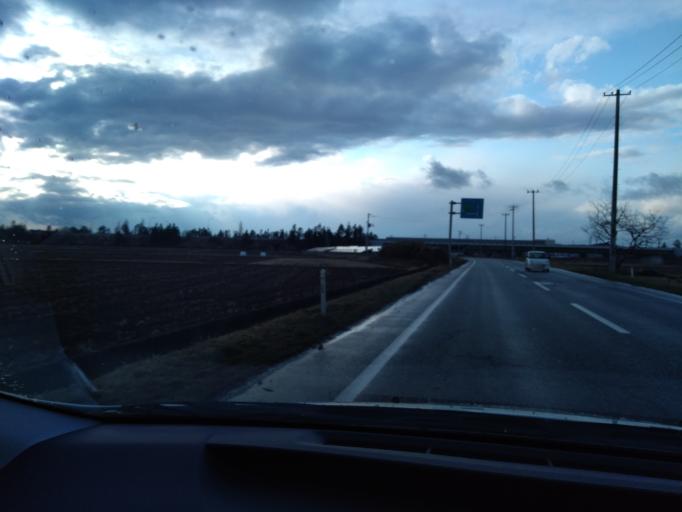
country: JP
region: Iwate
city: Ichinoseki
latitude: 38.7946
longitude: 141.0905
